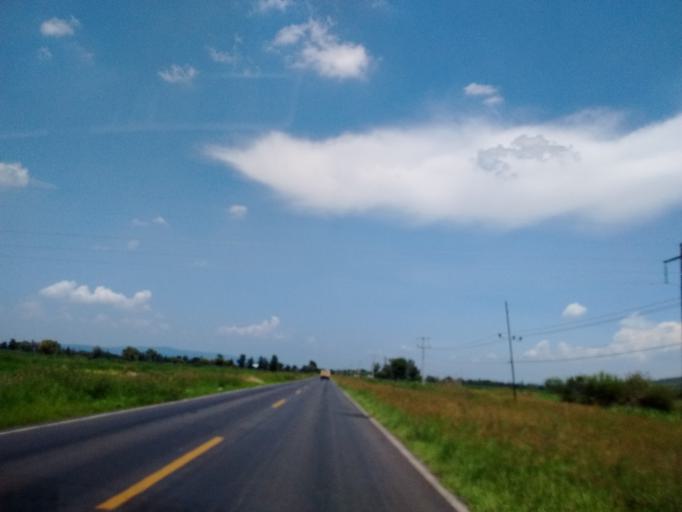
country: MX
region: Jalisco
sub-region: Atotonilco el Alto
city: Vistas del Maguey [Fraccionamiento]
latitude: 20.4958
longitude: -102.5243
